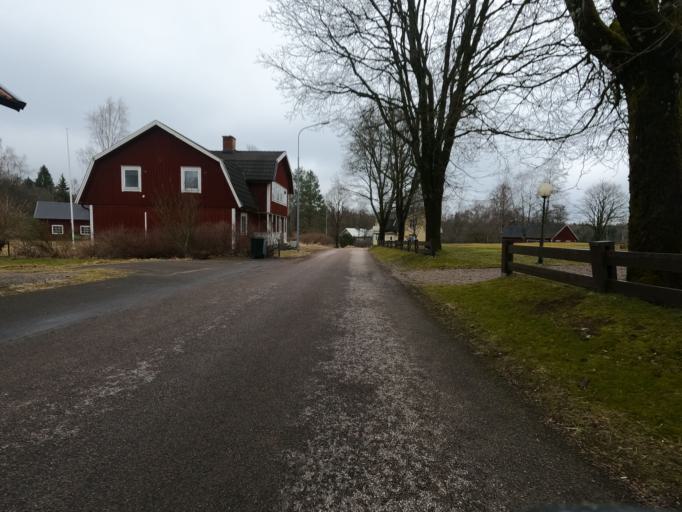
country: SE
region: Kronoberg
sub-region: Markaryds Kommun
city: Stromsnasbruk
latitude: 56.7901
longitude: 13.5683
